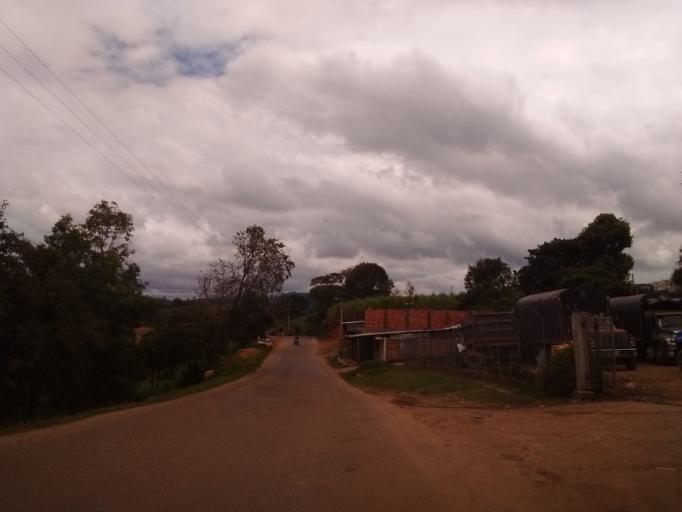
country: CO
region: Huila
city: Isnos
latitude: 1.9374
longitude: -76.2193
